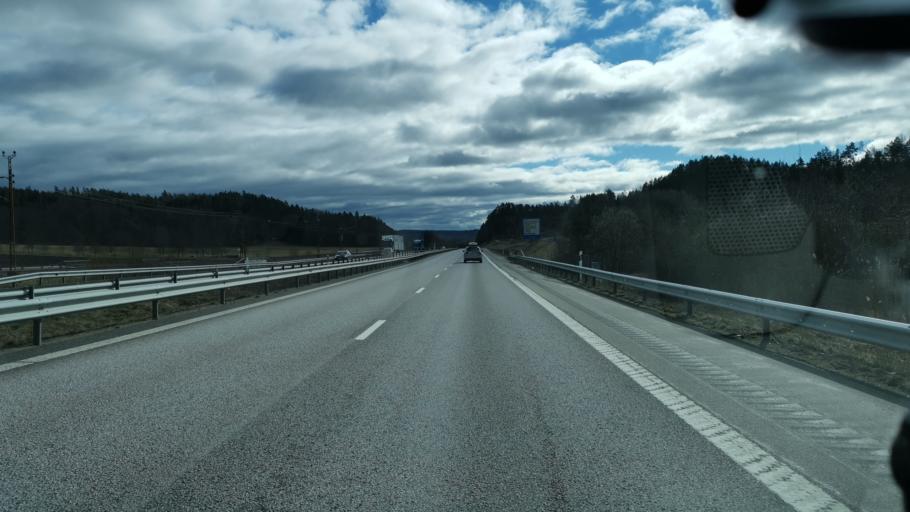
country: SE
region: Vaestra Goetaland
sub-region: Uddevalla Kommun
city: Ljungskile
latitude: 58.2524
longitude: 11.9034
